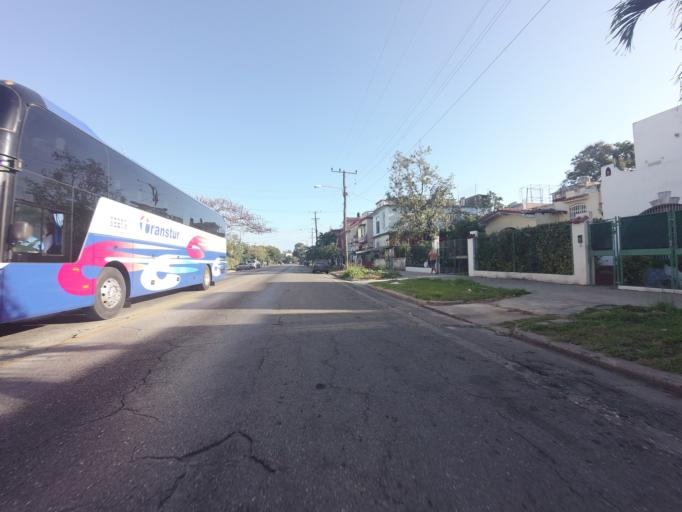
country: CU
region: La Habana
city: Havana
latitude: 23.1148
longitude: -82.4231
